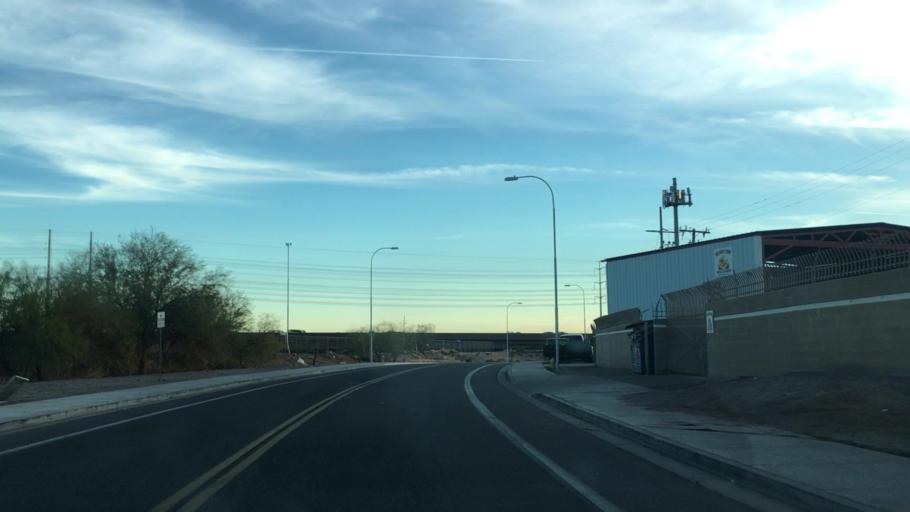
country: US
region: Arizona
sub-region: Maricopa County
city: Tempe
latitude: 33.4379
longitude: -111.9181
